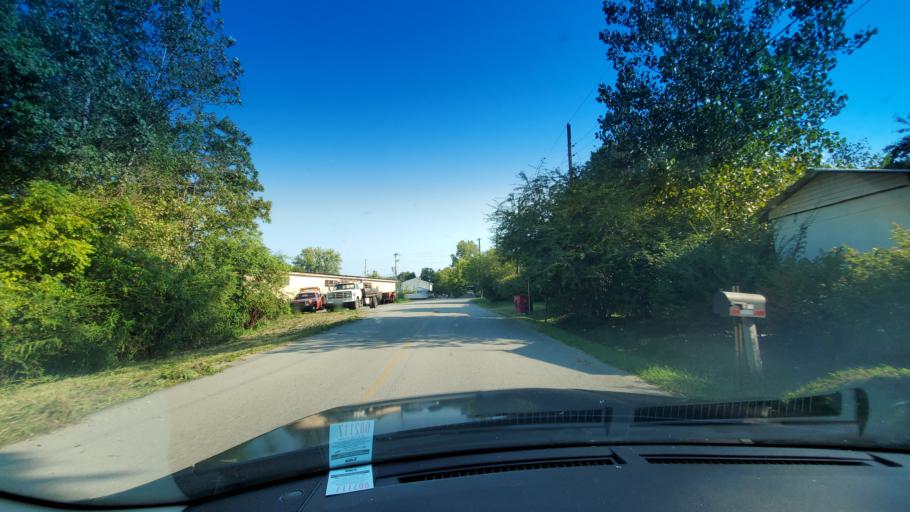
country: US
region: Tennessee
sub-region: Smith County
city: Carthage
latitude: 36.2533
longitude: -85.9563
